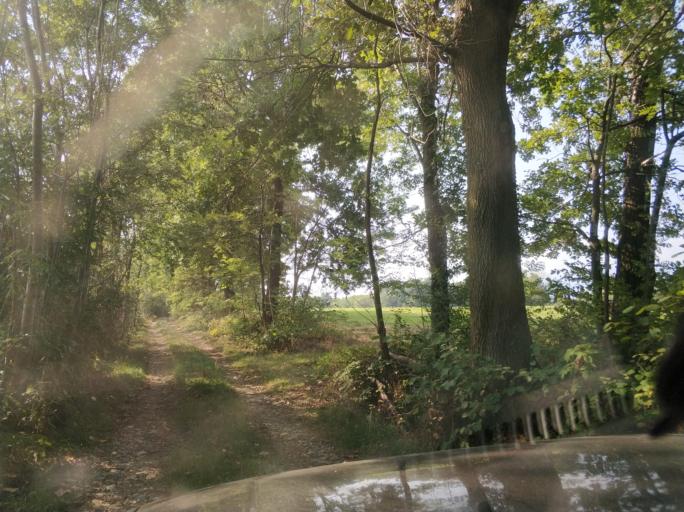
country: IT
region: Piedmont
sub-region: Provincia di Torino
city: San Carlo Canavese
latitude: 45.2618
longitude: 7.5882
